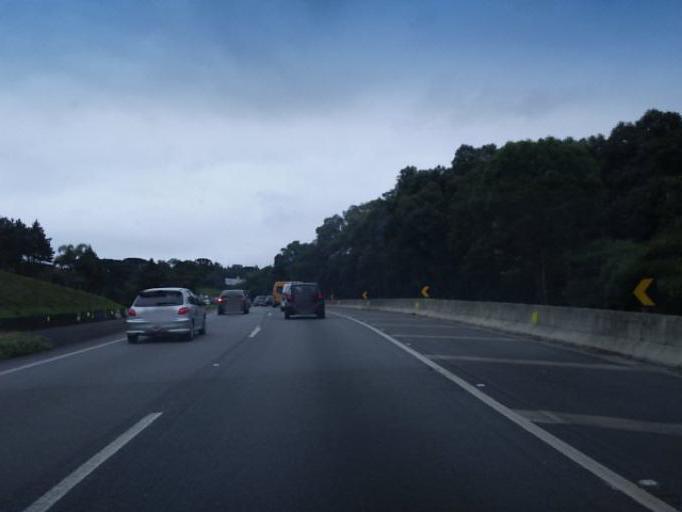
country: BR
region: Parana
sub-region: Sao Jose Dos Pinhais
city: Sao Jose dos Pinhais
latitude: -25.8435
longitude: -49.0601
